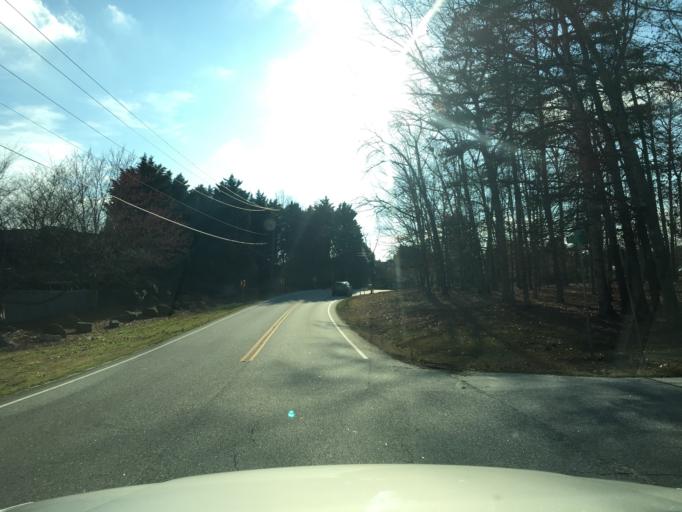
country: US
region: South Carolina
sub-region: Greenville County
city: Taylors
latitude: 34.8757
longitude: -82.2966
